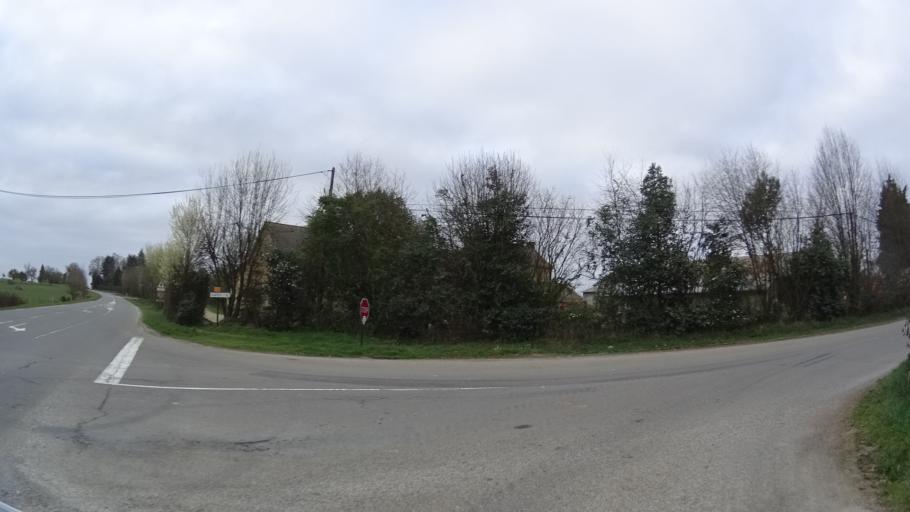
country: FR
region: Brittany
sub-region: Departement d'Ille-et-Vilaine
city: Saint-Gilles
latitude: 48.1746
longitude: -1.8465
